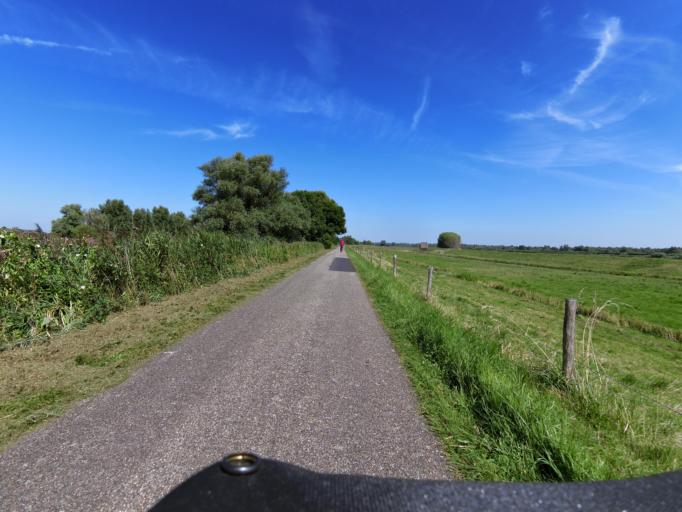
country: NL
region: North Brabant
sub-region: Gemeente Made en Drimmelen
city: Drimmelen
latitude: 51.7480
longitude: 4.7368
